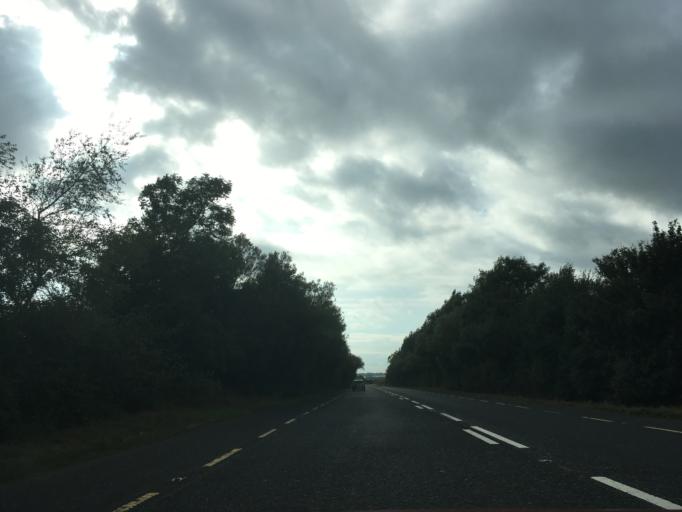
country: IE
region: Leinster
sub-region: Loch Garman
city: Loch Garman
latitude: 52.3440
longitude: -6.5875
